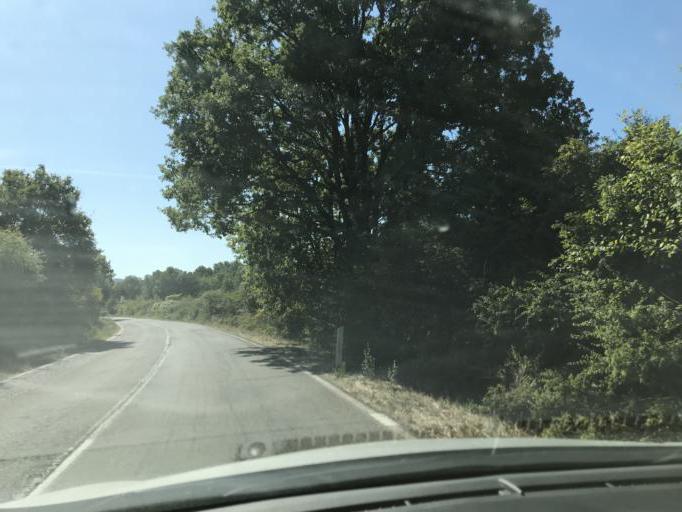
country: IT
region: Umbria
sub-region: Provincia di Terni
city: Avigliano Umbro
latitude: 42.6132
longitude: 12.4313
